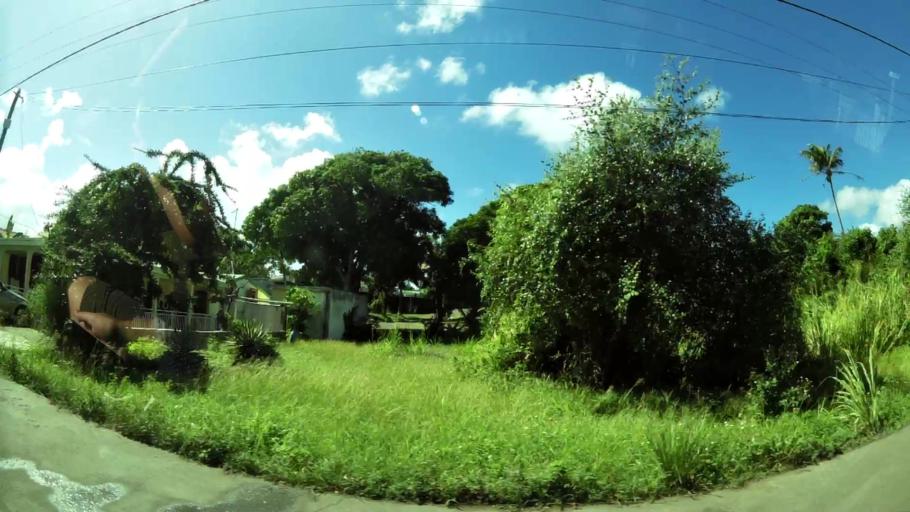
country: GP
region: Guadeloupe
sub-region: Guadeloupe
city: Petit-Canal
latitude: 16.3917
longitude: -61.4609
